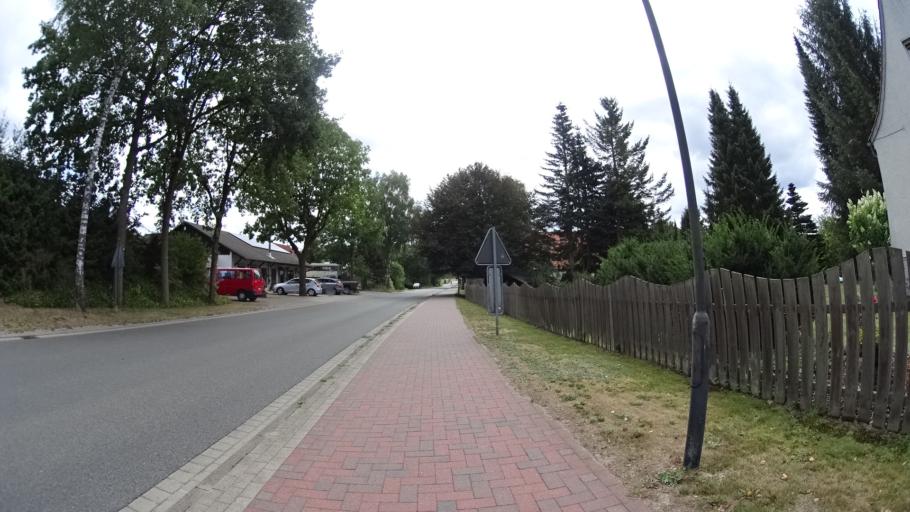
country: DE
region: Lower Saxony
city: Handeloh
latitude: 53.2419
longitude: 9.8475
